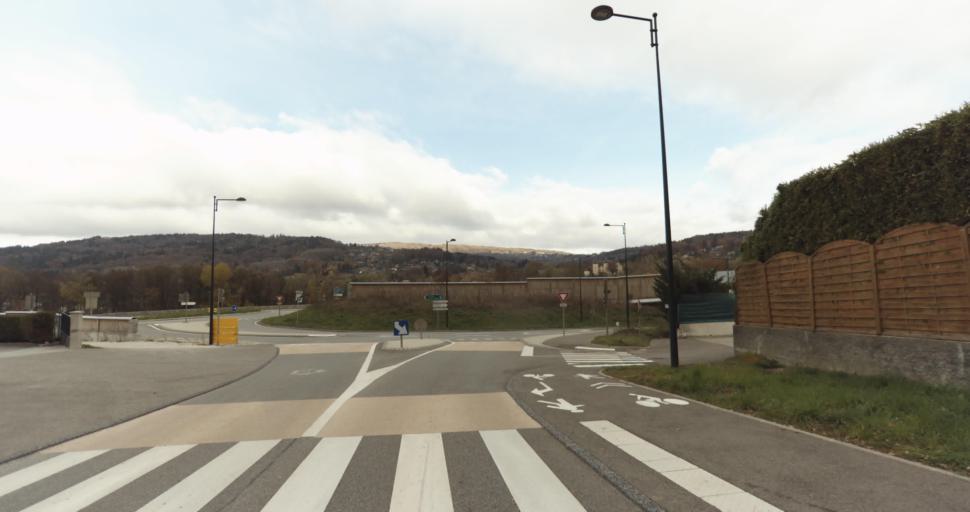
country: FR
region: Rhone-Alpes
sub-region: Departement de la Haute-Savoie
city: Pringy
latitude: 45.9497
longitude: 6.1155
